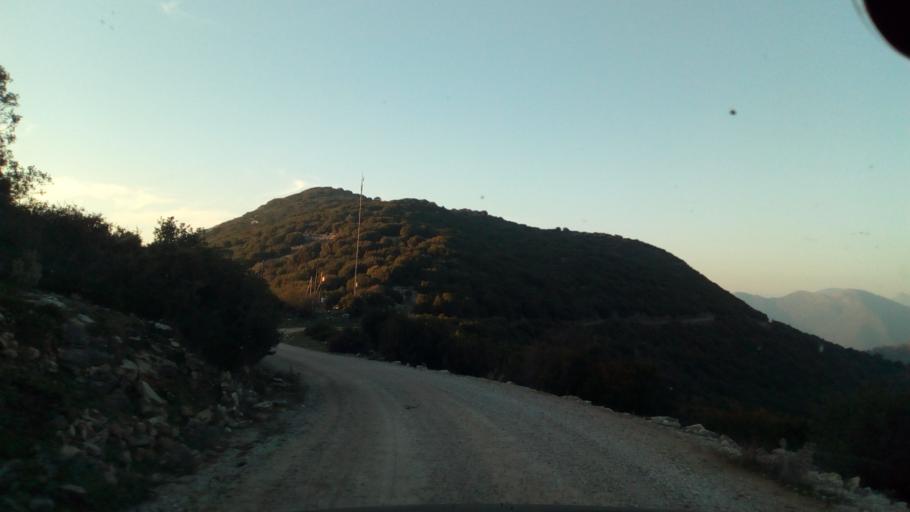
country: GR
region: West Greece
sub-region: Nomos Aitolias kai Akarnanias
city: Nafpaktos
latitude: 38.4680
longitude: 21.8242
